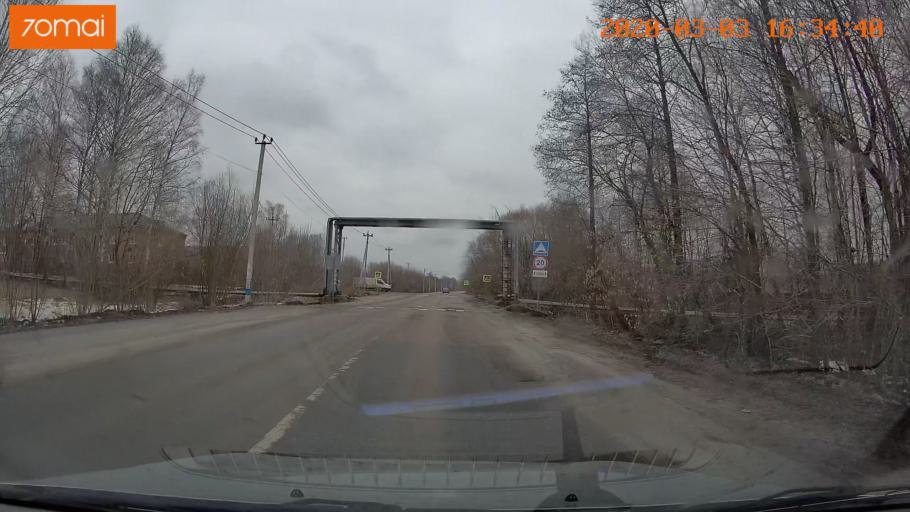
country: RU
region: Moskovskaya
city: Lopatinskiy
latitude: 55.4070
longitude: 38.7599
